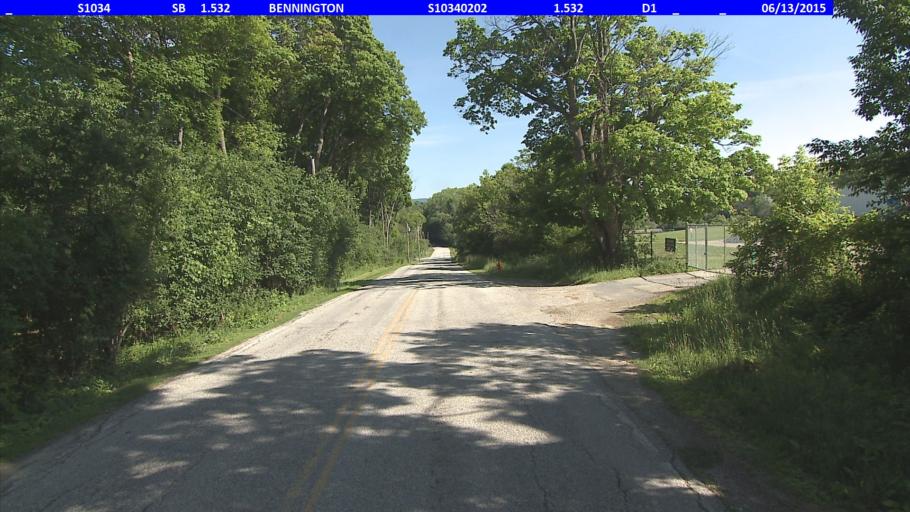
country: US
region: Vermont
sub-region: Bennington County
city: Bennington
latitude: 42.8725
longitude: -73.2124
